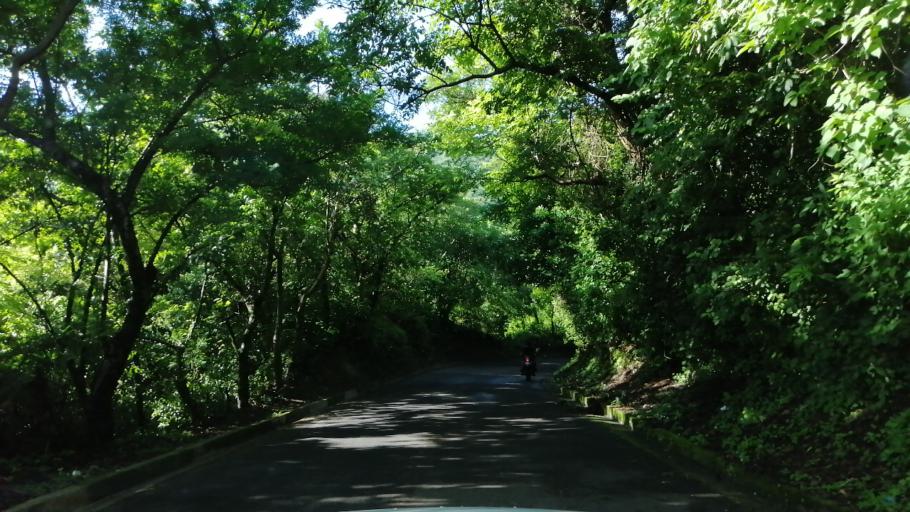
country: SV
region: Morazan
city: Cacaopera
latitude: 13.7709
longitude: -88.0738
